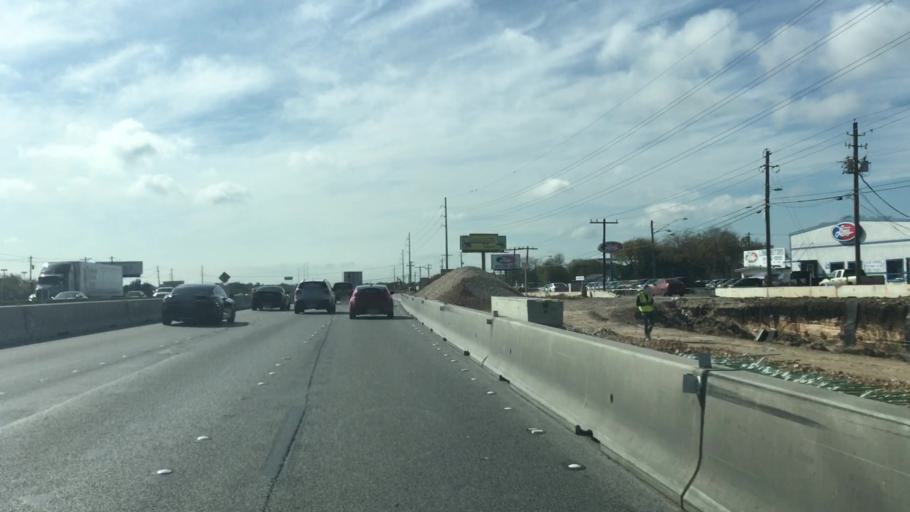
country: US
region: Texas
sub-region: Travis County
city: Onion Creek
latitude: 30.1880
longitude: -97.7728
